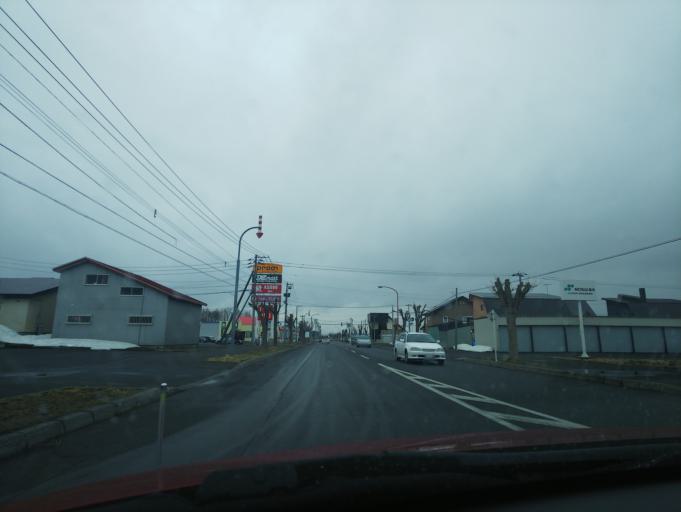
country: JP
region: Hokkaido
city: Nayoro
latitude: 44.3376
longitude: 142.4503
